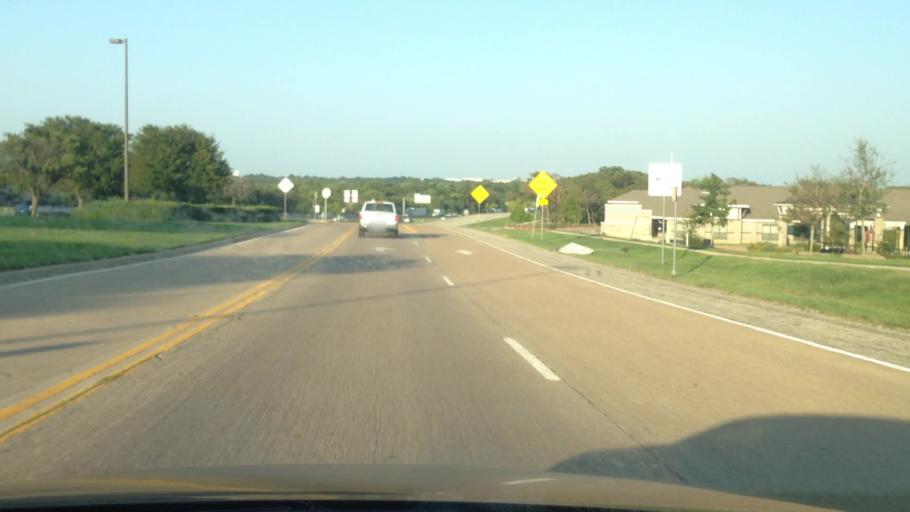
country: US
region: Texas
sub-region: Tarrant County
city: Dalworthington Gardens
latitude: 32.6734
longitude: -97.1644
